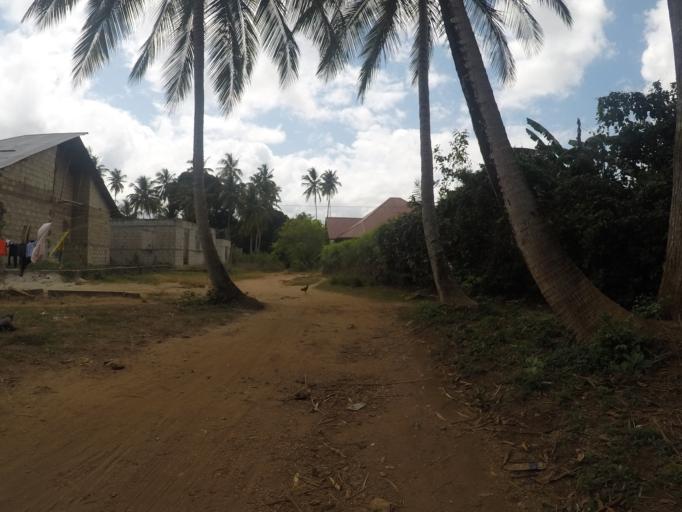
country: TZ
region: Zanzibar Urban/West
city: Zanzibar
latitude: -6.2062
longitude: 39.2340
